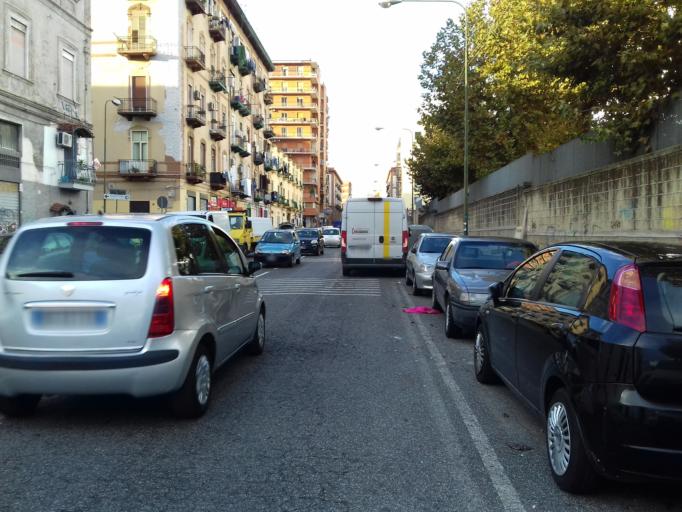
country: IT
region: Campania
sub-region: Provincia di Napoli
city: Napoli
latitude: 40.8615
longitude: 14.2731
